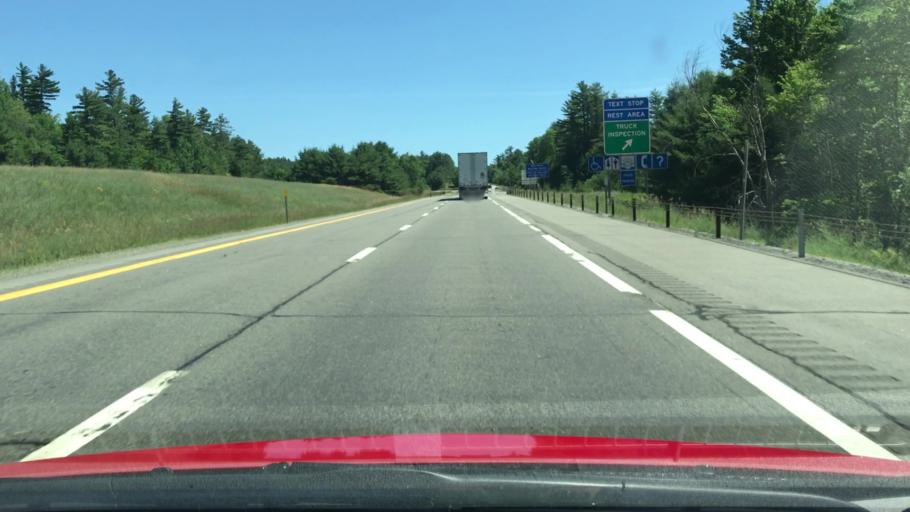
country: US
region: New York
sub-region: Essex County
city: Mineville
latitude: 44.0093
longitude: -73.7129
